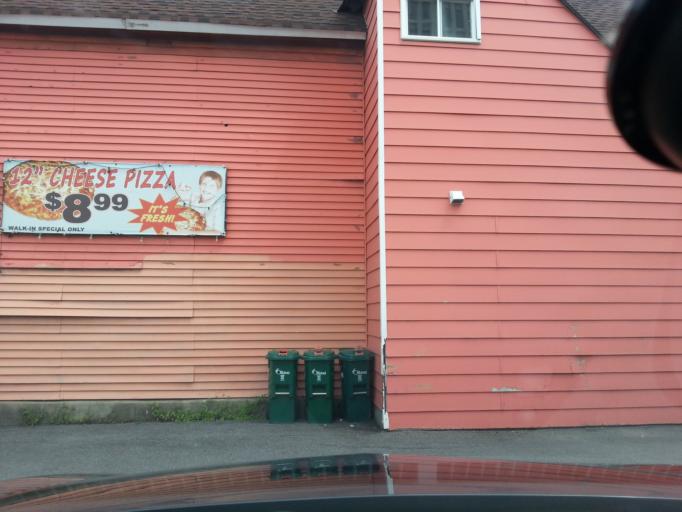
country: CA
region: Ontario
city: Ottawa
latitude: 45.4098
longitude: -75.6884
